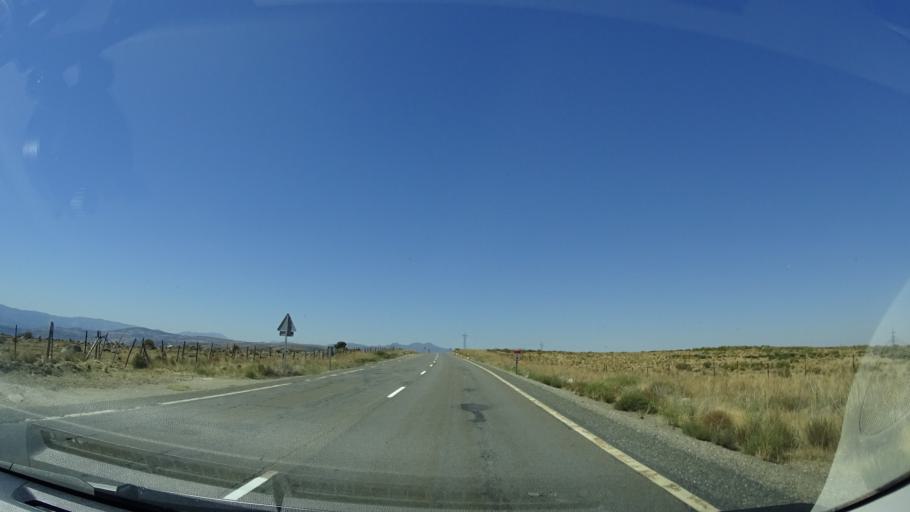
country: ES
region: Castille and Leon
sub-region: Provincia de Avila
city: Santa Cruz de Pinares
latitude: 40.6090
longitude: -4.5352
